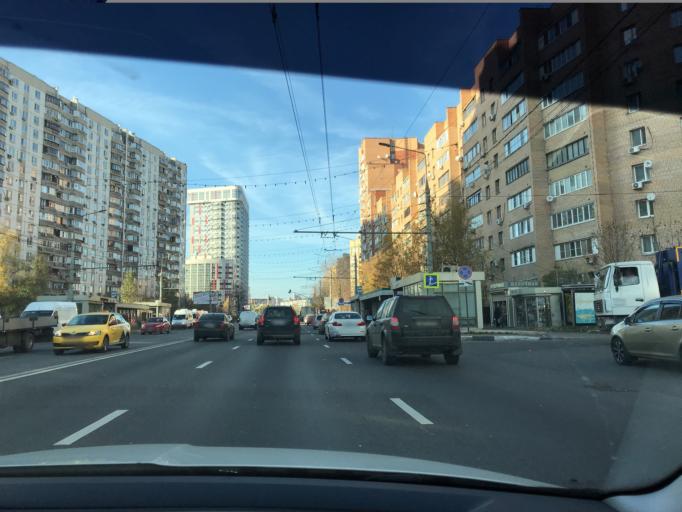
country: RU
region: Moscow
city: Khimki
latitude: 55.8788
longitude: 37.4225
